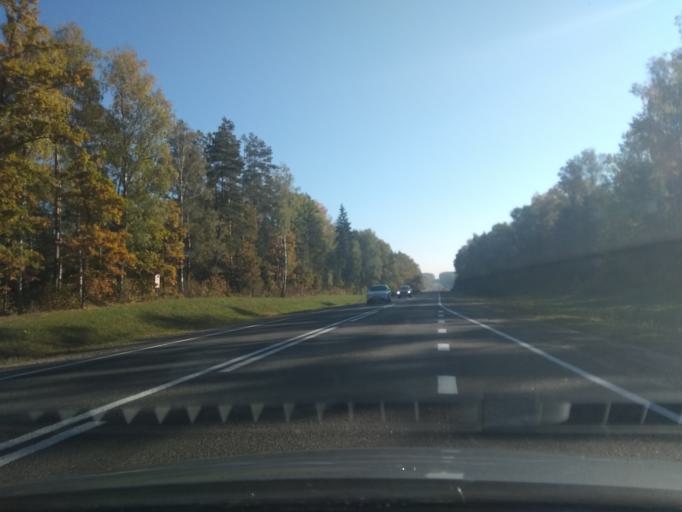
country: BY
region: Grodnenskaya
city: Zel'va
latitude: 53.1401
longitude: 24.9103
